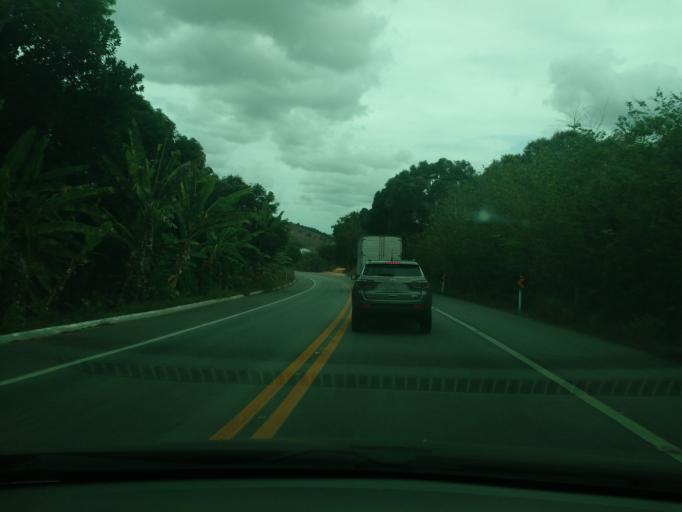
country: BR
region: Alagoas
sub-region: Uniao Dos Palmares
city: Uniao dos Palmares
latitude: -9.2301
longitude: -36.0268
